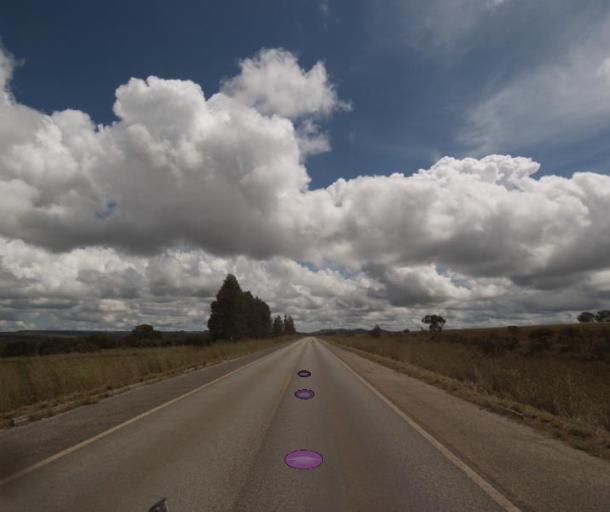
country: BR
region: Goias
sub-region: Pirenopolis
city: Pirenopolis
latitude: -15.7498
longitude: -48.6531
